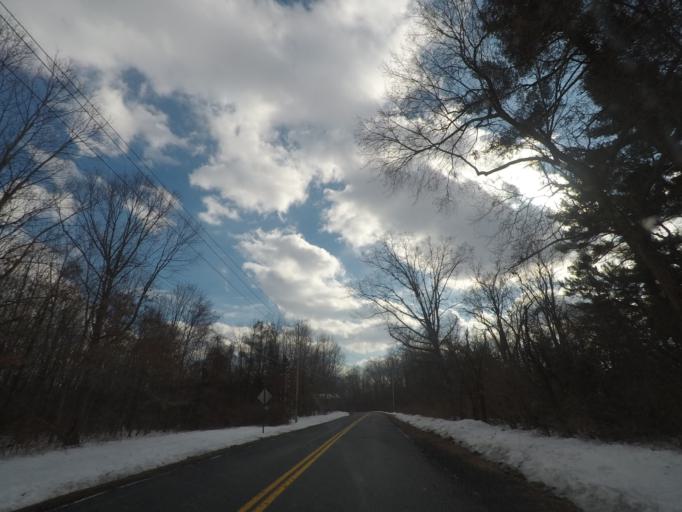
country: US
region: New York
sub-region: Schenectady County
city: Niskayuna
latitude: 42.8230
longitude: -73.8557
